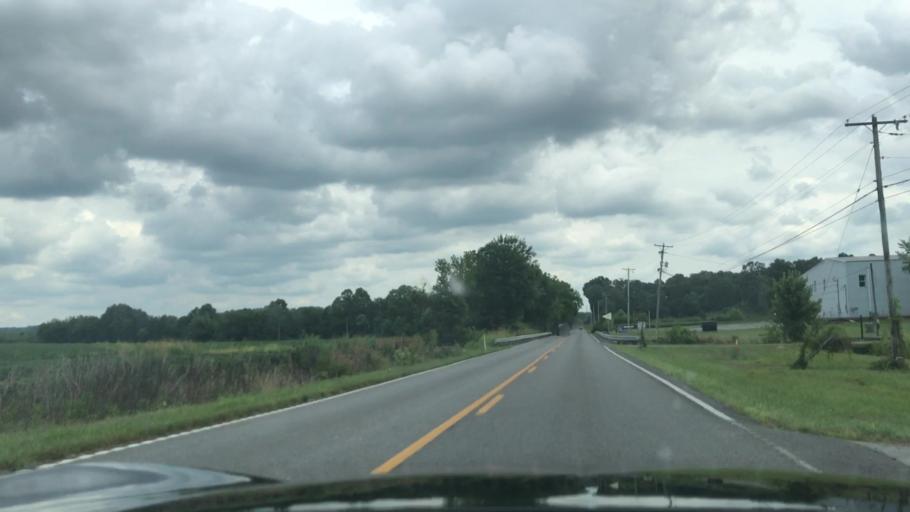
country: US
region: Kentucky
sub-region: Muhlenberg County
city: Greenville
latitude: 37.1975
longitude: -87.1252
